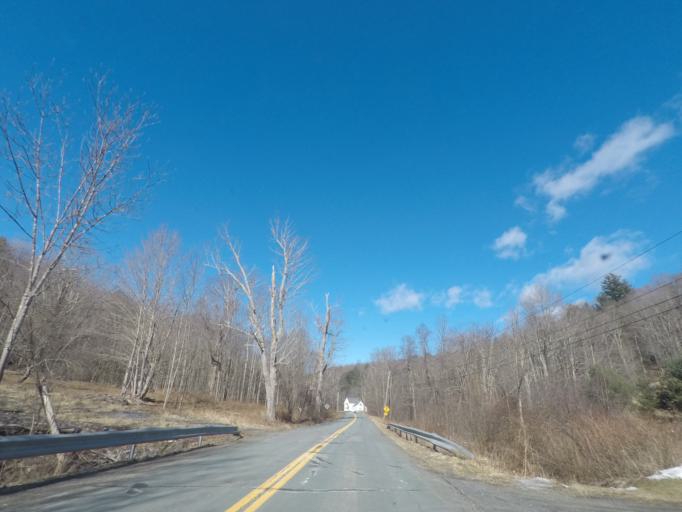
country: US
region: Massachusetts
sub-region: Berkshire County
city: Williamstown
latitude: 42.7408
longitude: -73.3375
